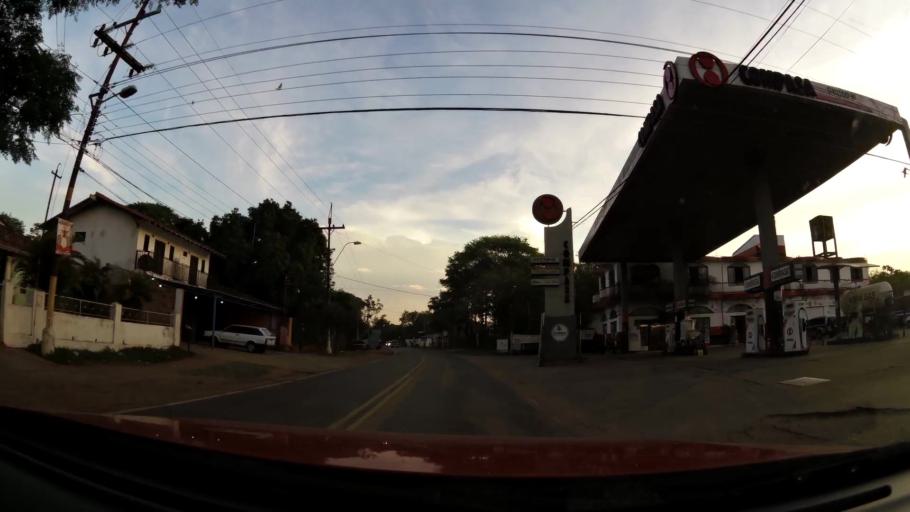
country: PY
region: Central
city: San Lorenzo
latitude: -25.3575
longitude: -57.4910
